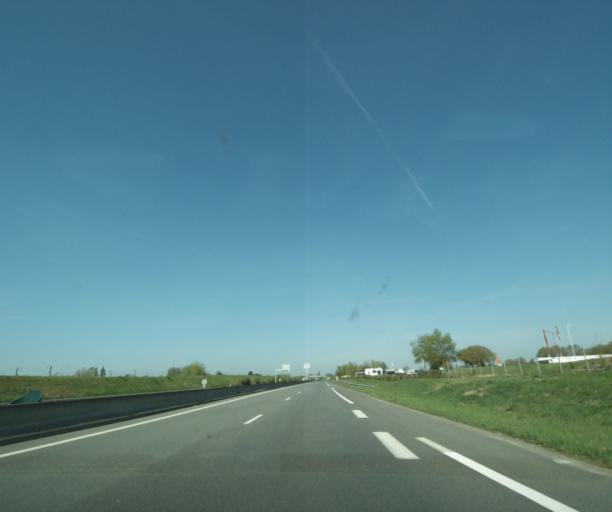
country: FR
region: Auvergne
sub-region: Departement de l'Allier
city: Avermes
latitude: 46.5994
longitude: 3.3063
